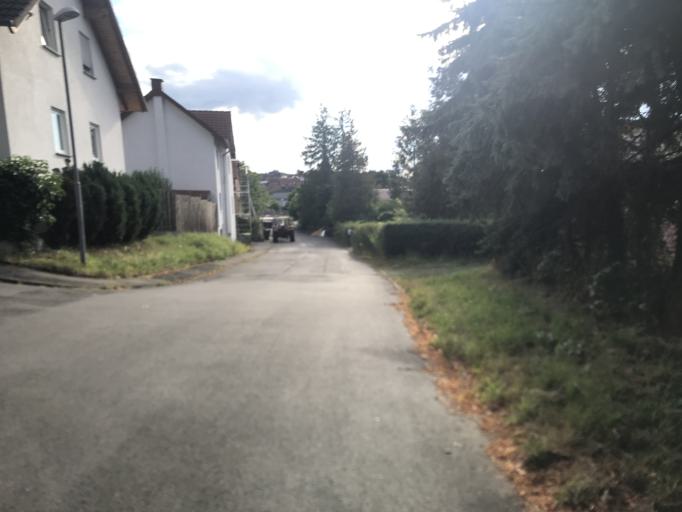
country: DE
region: Hesse
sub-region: Regierungsbezirk Giessen
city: Lohra
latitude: 50.6737
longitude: 8.5776
